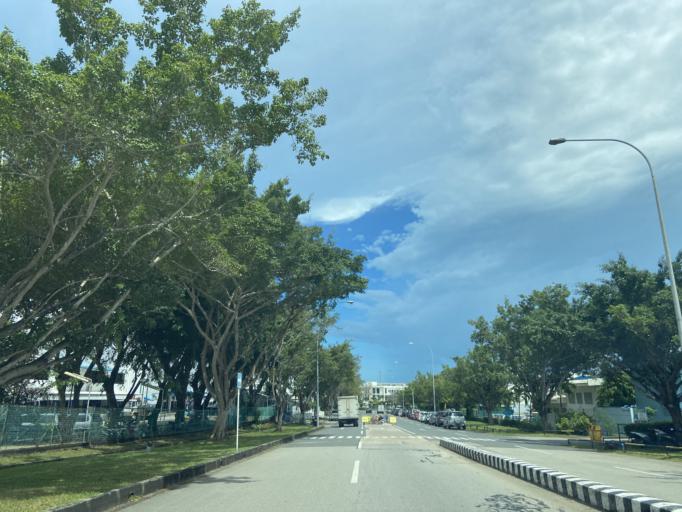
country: SG
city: Singapore
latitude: 1.0647
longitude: 104.0319
